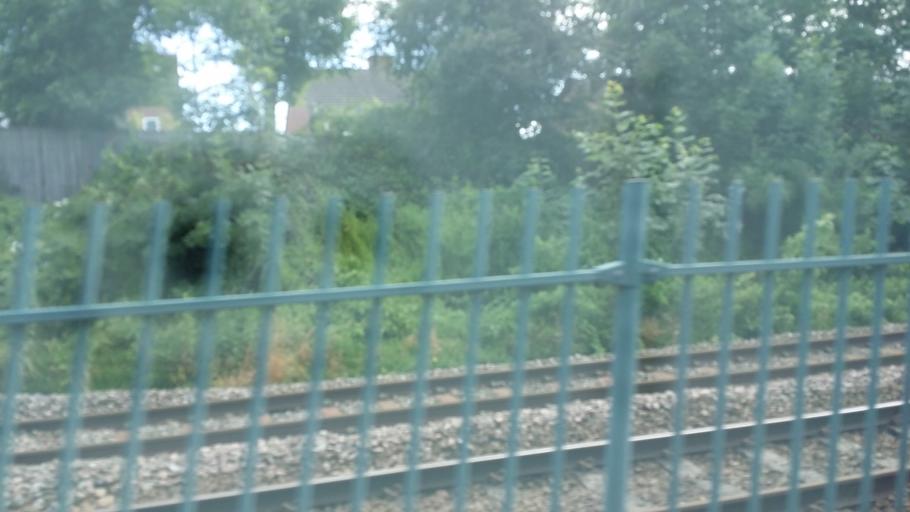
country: GB
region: England
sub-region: Nottinghamshire
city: Hucknall
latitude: 52.9900
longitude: -1.1900
